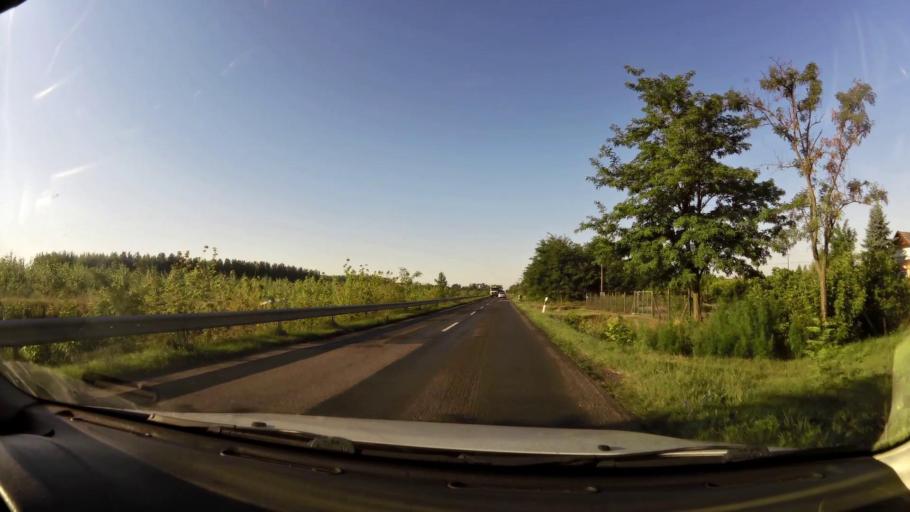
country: HU
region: Pest
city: Tapioszolos
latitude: 47.2797
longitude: 19.8658
